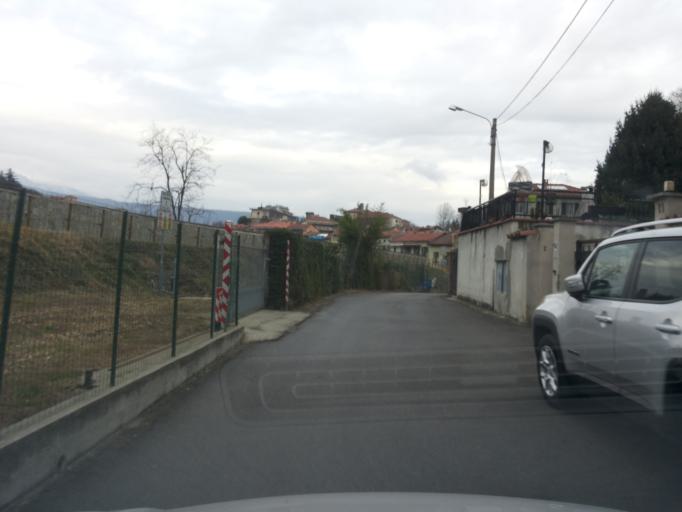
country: IT
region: Piedmont
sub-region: Provincia di Torino
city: Ivrea
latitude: 45.4634
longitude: 7.8684
